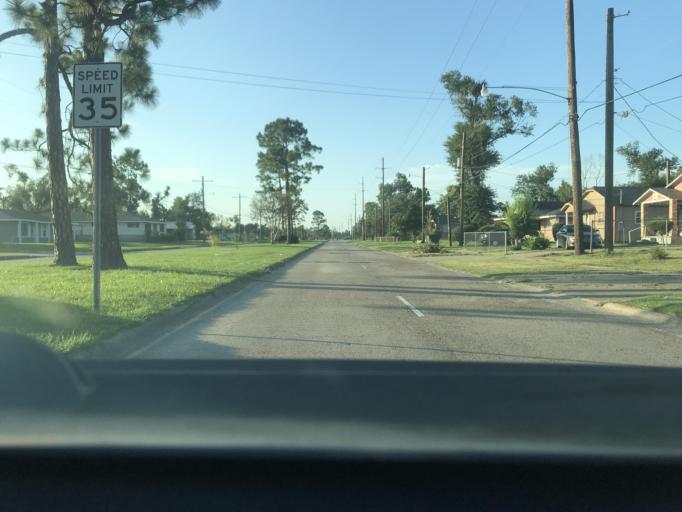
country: US
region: Louisiana
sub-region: Calcasieu Parish
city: Lake Charles
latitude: 30.2500
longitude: -93.1952
